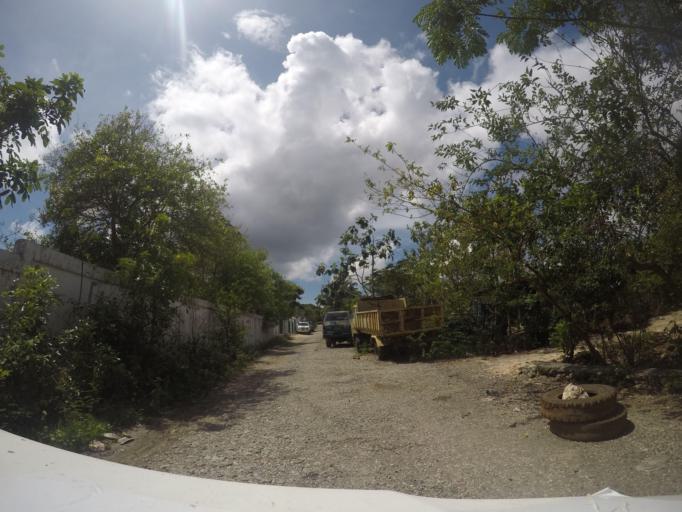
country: TL
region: Baucau
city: Baucau
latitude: -8.4724
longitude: 126.4570
